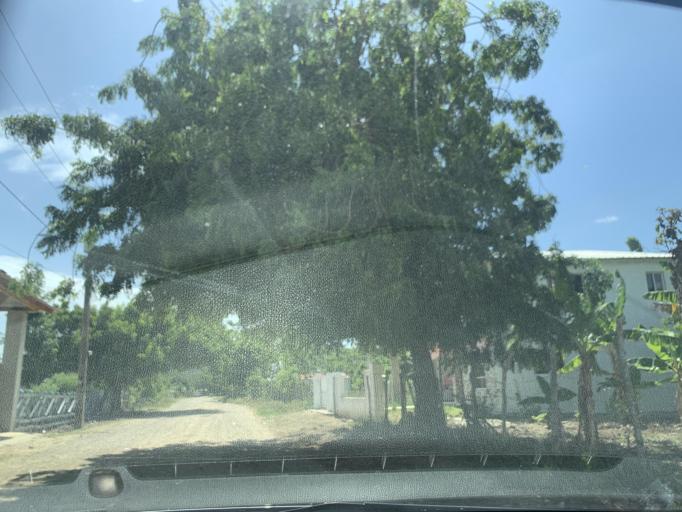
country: DO
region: Puerto Plata
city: Luperon
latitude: 19.8901
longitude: -70.8831
